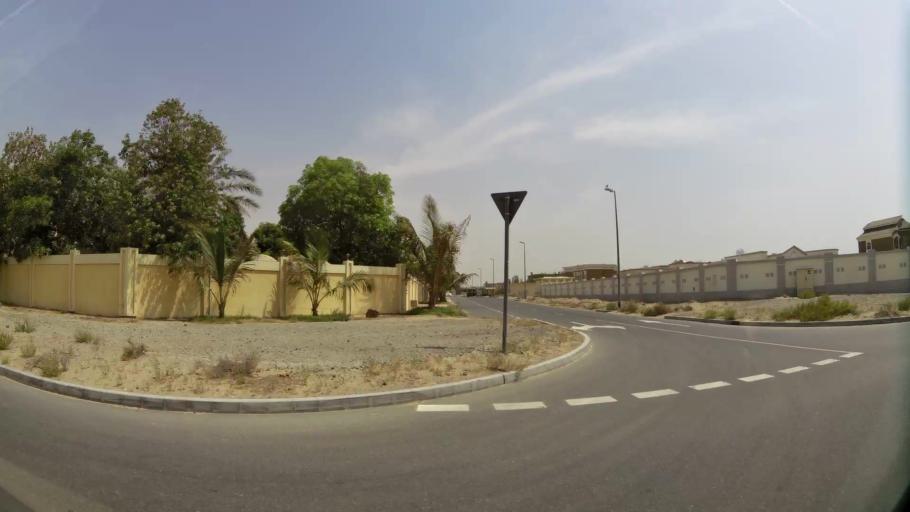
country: AE
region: Ash Shariqah
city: Sharjah
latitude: 25.2594
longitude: 55.4729
